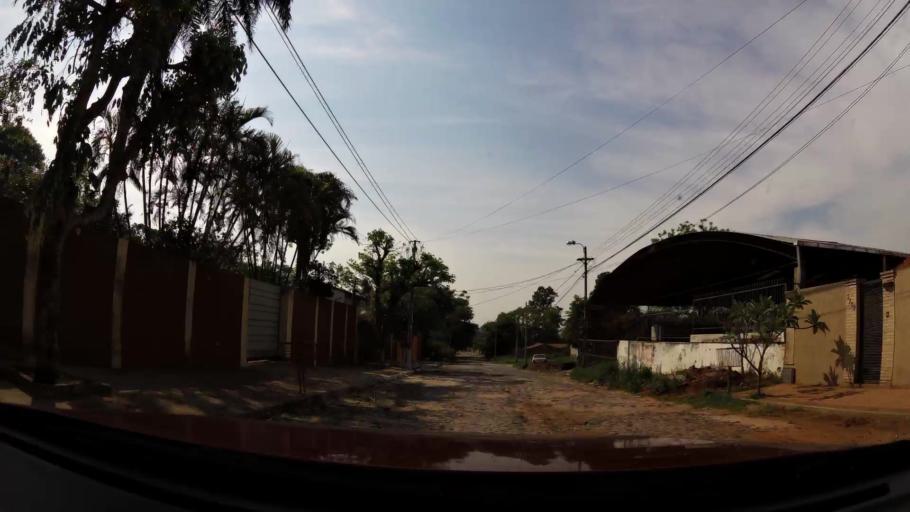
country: PY
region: Central
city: Fernando de la Mora
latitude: -25.2609
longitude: -57.5520
